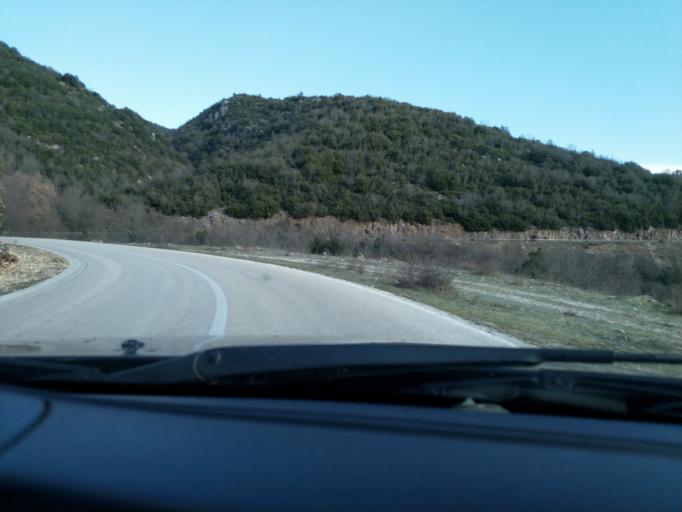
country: GR
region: Epirus
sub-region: Nomos Ioanninon
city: Asprangeloi
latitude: 39.8677
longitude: 20.7381
